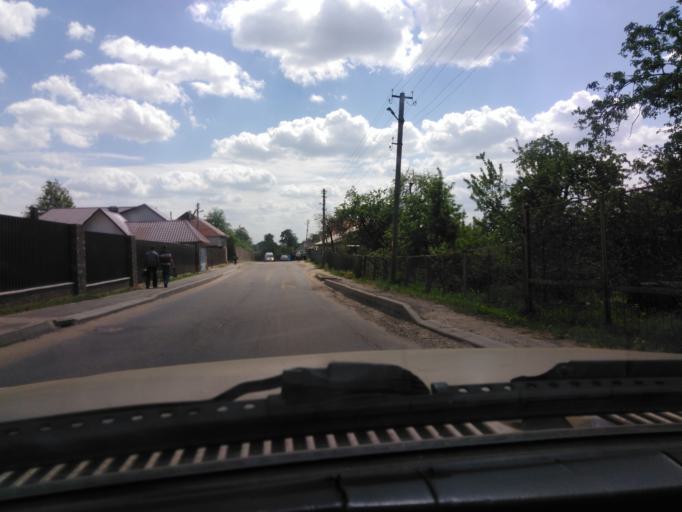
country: BY
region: Mogilev
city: Mahilyow
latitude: 53.9349
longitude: 30.3241
